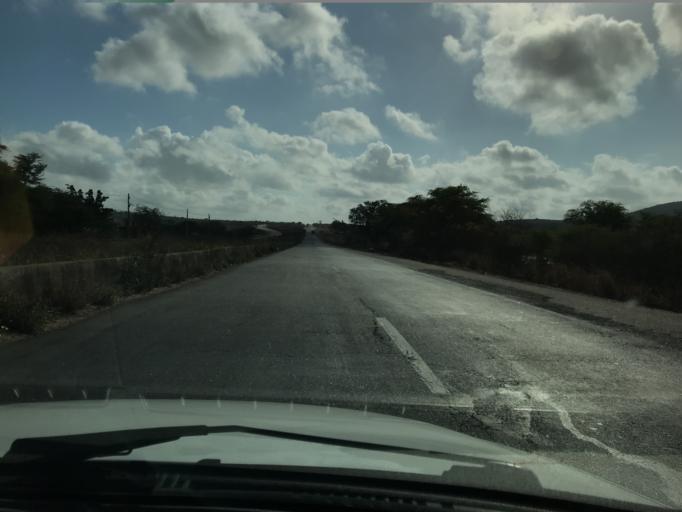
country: BR
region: Pernambuco
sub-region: Bezerros
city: Bezerros
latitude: -8.2300
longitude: -35.7051
